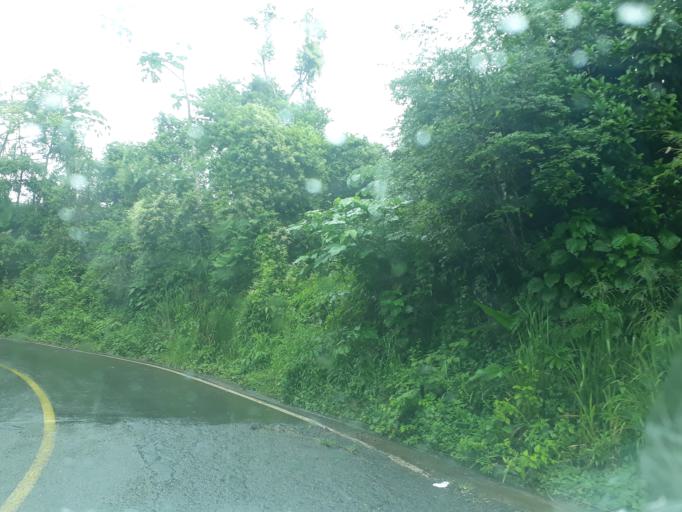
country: CO
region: Cundinamarca
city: Paratebueno
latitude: 4.3984
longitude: -73.3036
